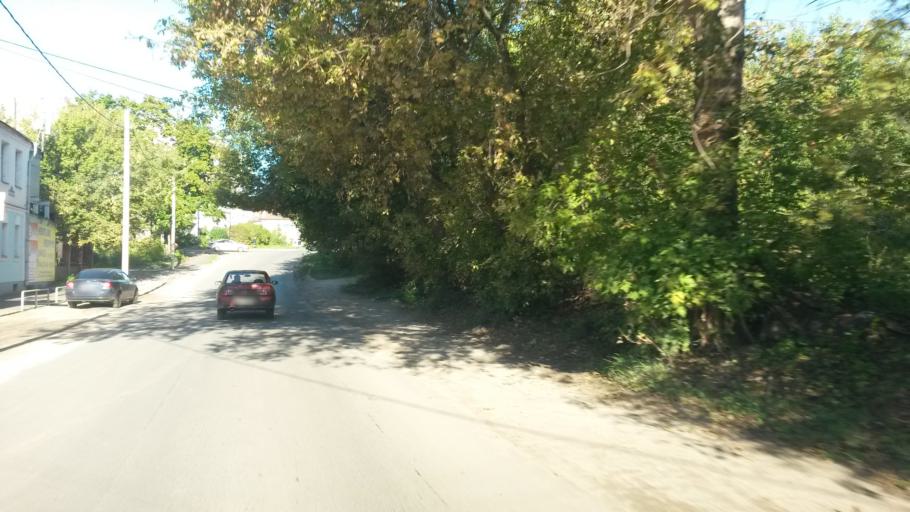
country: RU
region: Ivanovo
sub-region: Gorod Ivanovo
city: Ivanovo
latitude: 56.9903
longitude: 40.9790
